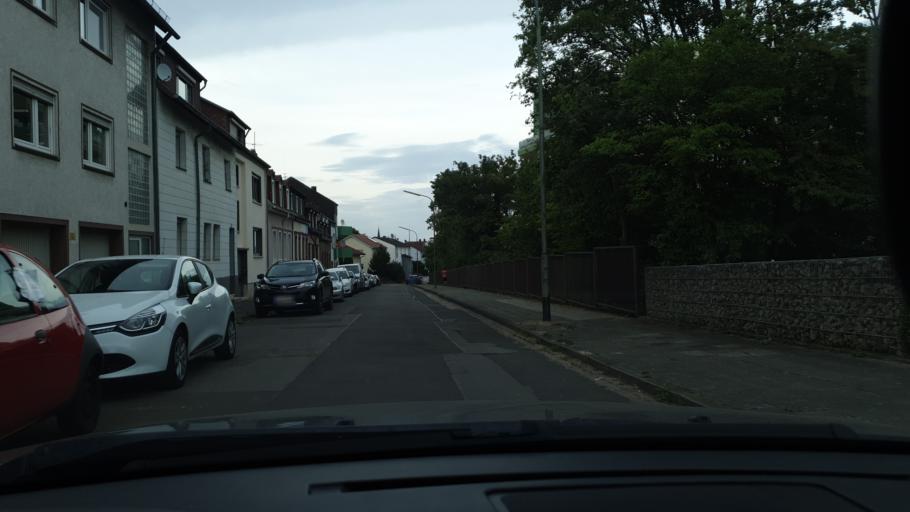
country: DE
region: Rheinland-Pfalz
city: Kaiserslautern
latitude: 49.4313
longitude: 7.7500
